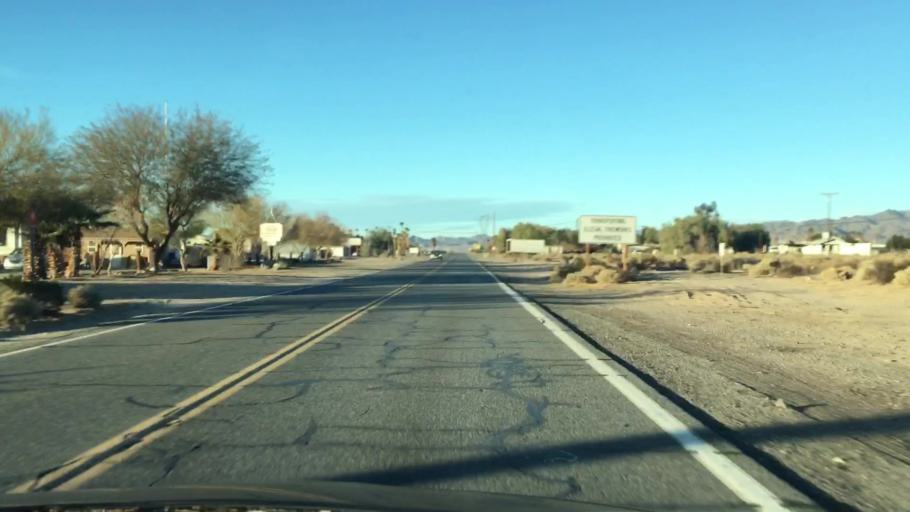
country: US
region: California
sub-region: San Bernardino County
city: Fort Irwin
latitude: 35.2697
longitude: -116.0750
